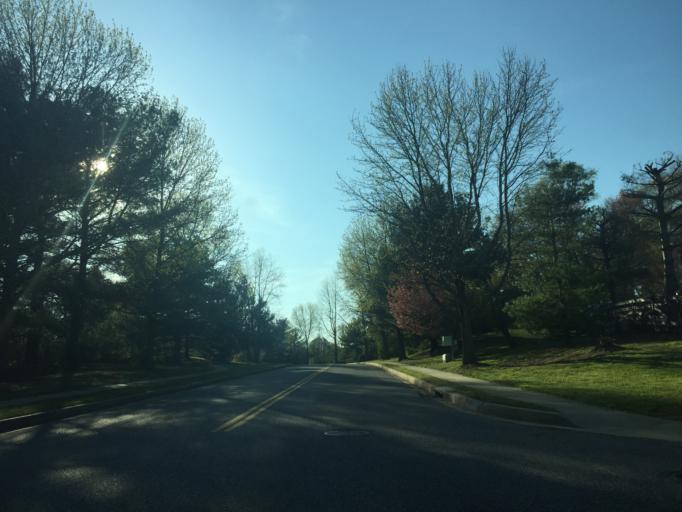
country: US
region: Maryland
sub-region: Harford County
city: Riverside
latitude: 39.4722
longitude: -76.2437
